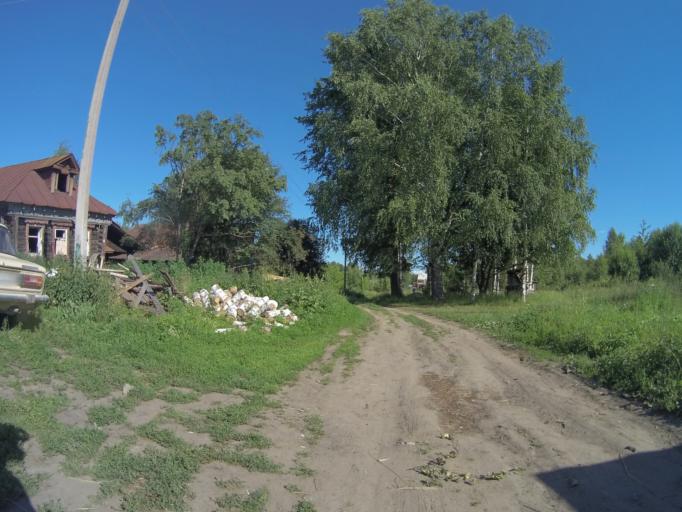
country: RU
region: Vladimir
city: Golovino
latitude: 56.0032
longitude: 40.3954
